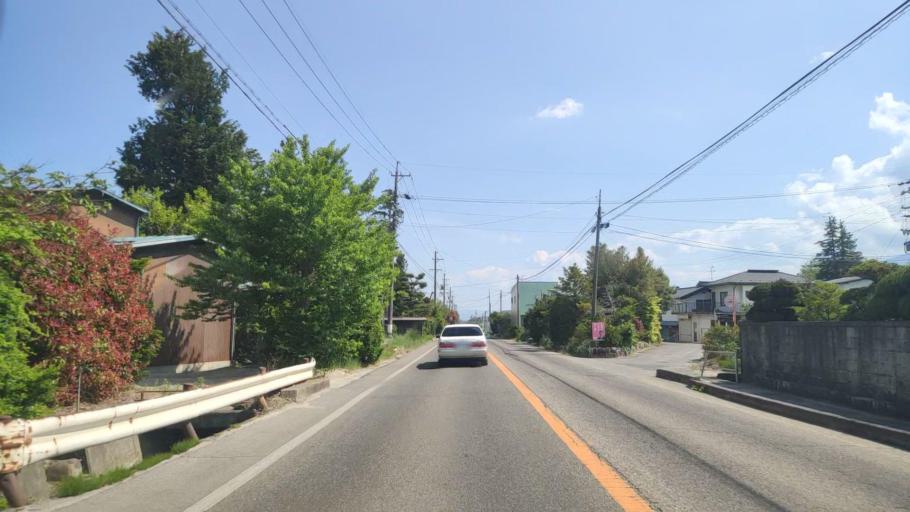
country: JP
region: Nagano
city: Hotaka
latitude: 36.3939
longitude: 137.8635
